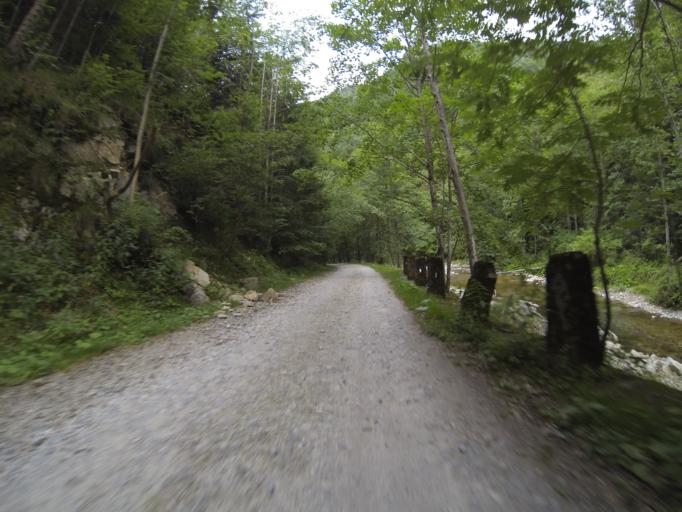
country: RO
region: Gorj
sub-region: Comuna Polovragi
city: Polovragi
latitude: 45.2509
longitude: 23.7651
